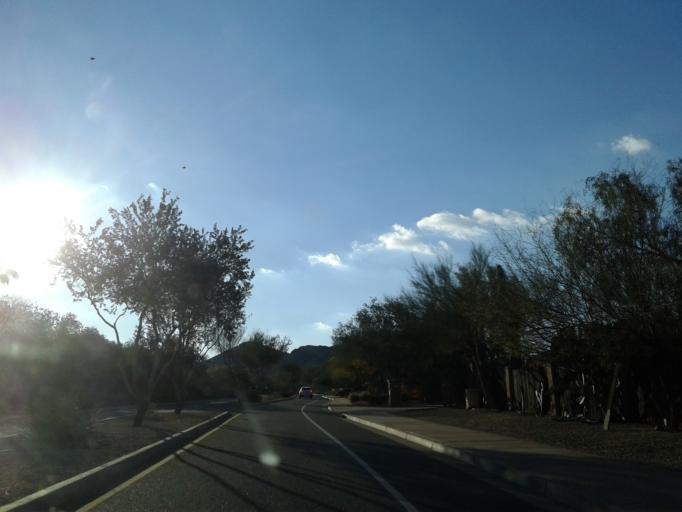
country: US
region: Arizona
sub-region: Maricopa County
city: Paradise Valley
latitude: 33.5682
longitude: -111.9675
